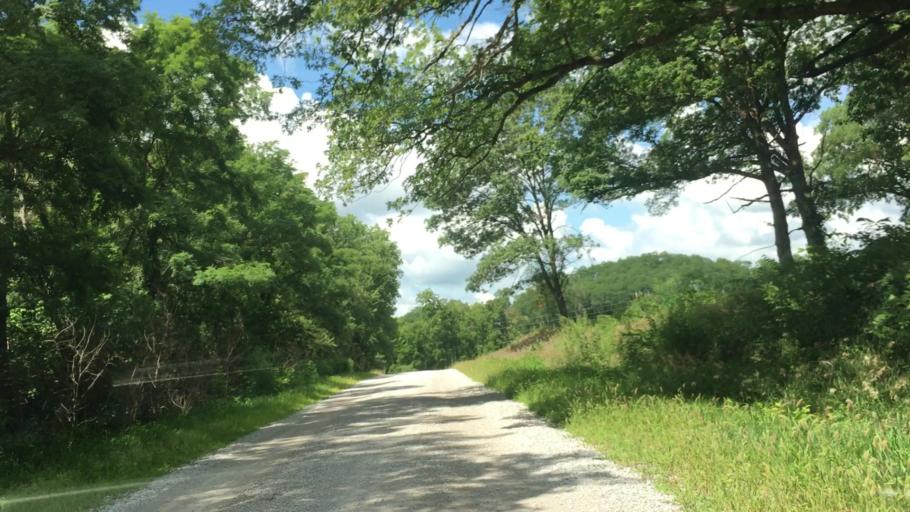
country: US
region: Iowa
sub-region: Linn County
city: Lisbon
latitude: 41.8288
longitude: -91.3828
